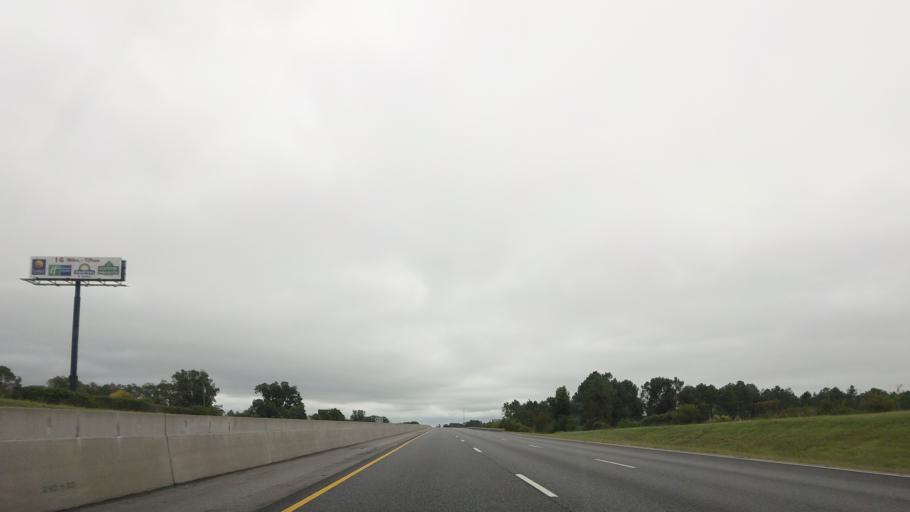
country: US
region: Georgia
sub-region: Turner County
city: Ashburn
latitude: 31.6622
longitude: -83.6050
